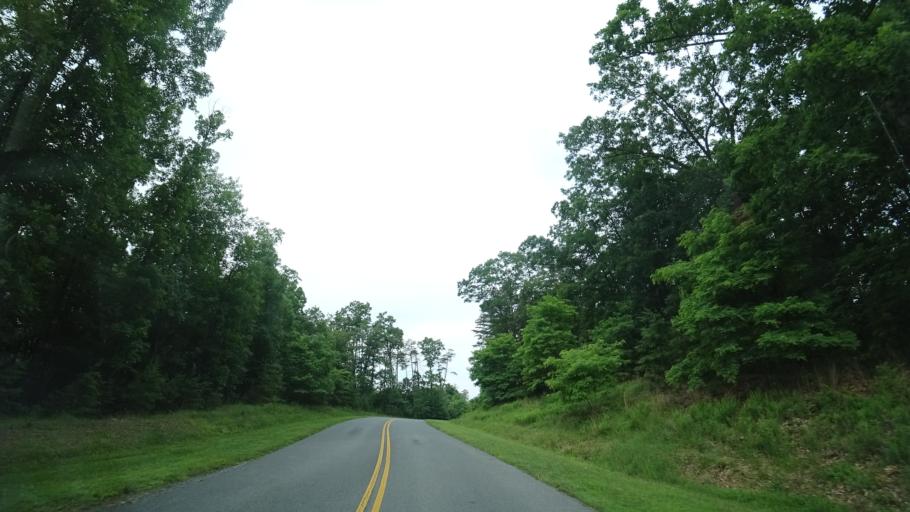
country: US
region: Virginia
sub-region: Warren County
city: Front Royal
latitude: 38.8484
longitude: -78.3048
